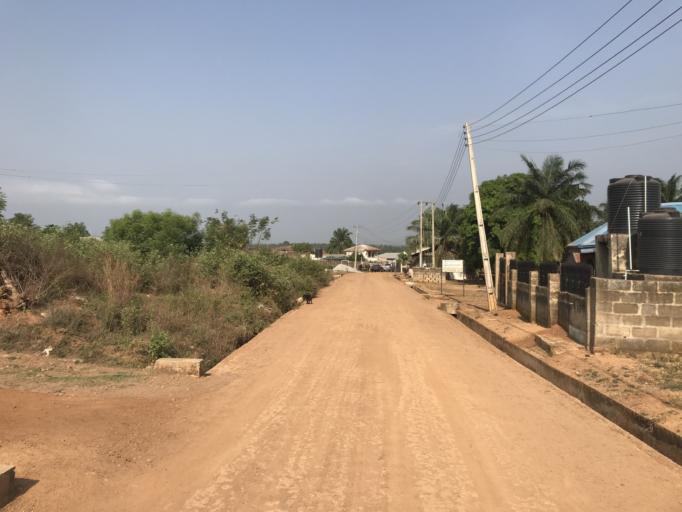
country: NG
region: Osun
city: Iwo
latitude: 7.6190
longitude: 4.1507
